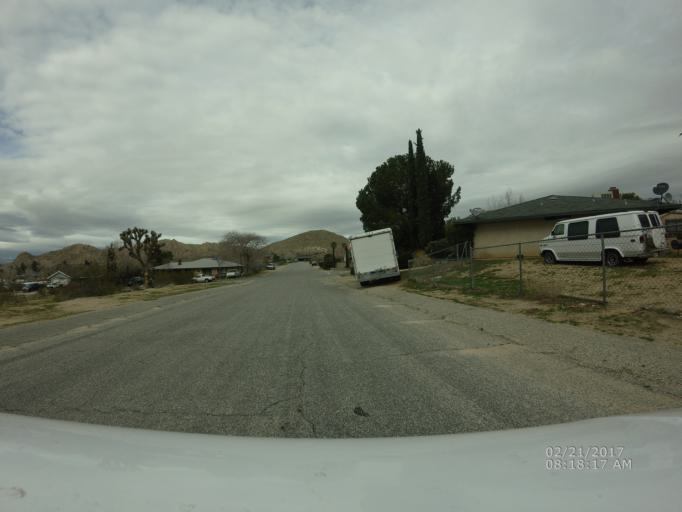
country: US
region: California
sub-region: Los Angeles County
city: Lake Los Angeles
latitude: 34.6015
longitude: -117.8397
